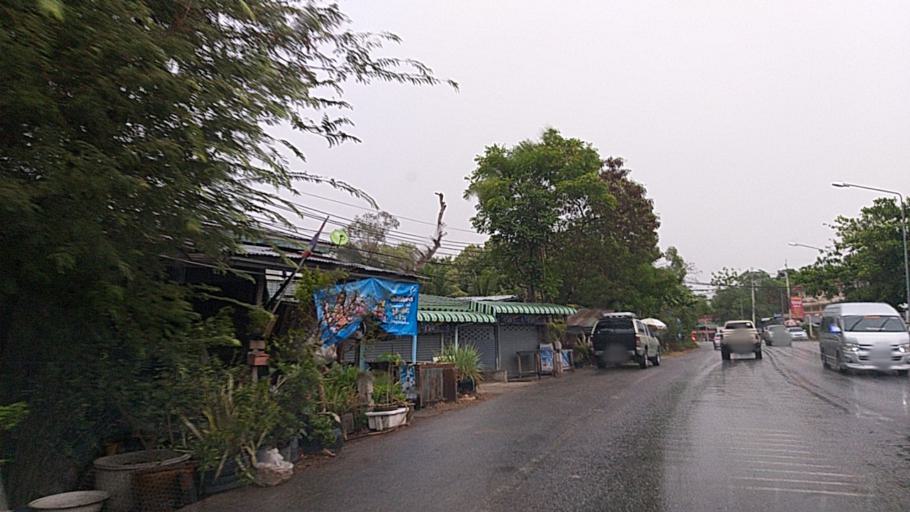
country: TH
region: Phra Nakhon Si Ayutthaya
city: Phra Nakhon Si Ayutthaya
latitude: 14.3433
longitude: 100.5806
